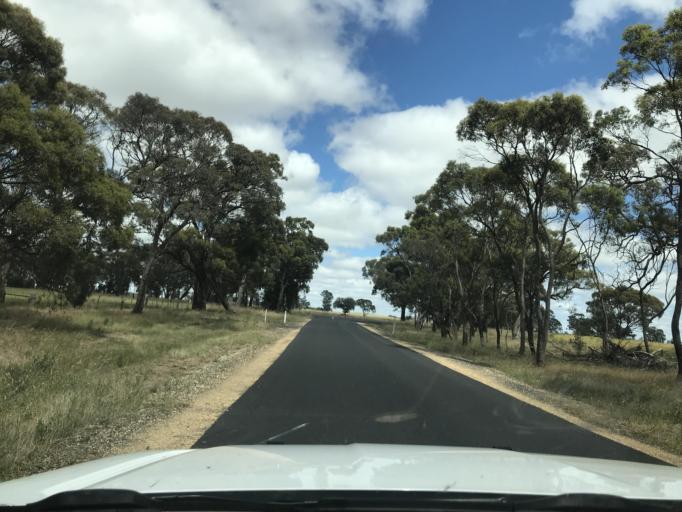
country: AU
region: South Australia
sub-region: Naracoorte and Lucindale
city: Naracoorte
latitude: -36.6688
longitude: 141.2749
